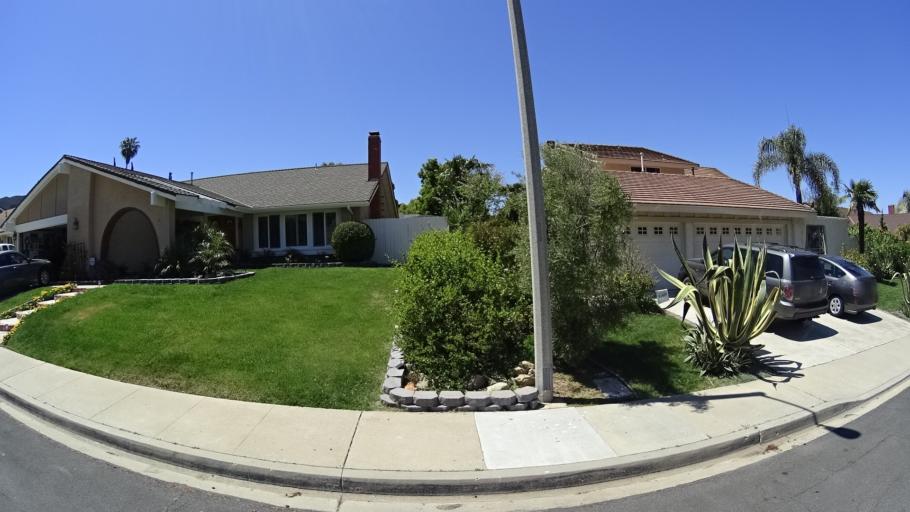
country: US
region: California
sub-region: Ventura County
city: Casa Conejo
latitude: 34.1817
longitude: -118.8968
